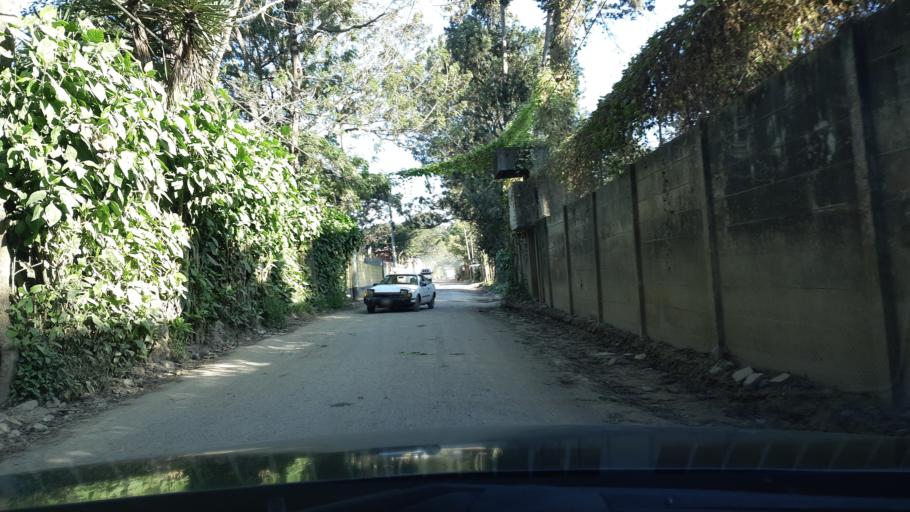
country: GT
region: Chimaltenango
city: El Tejar
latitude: 14.6398
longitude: -90.8063
